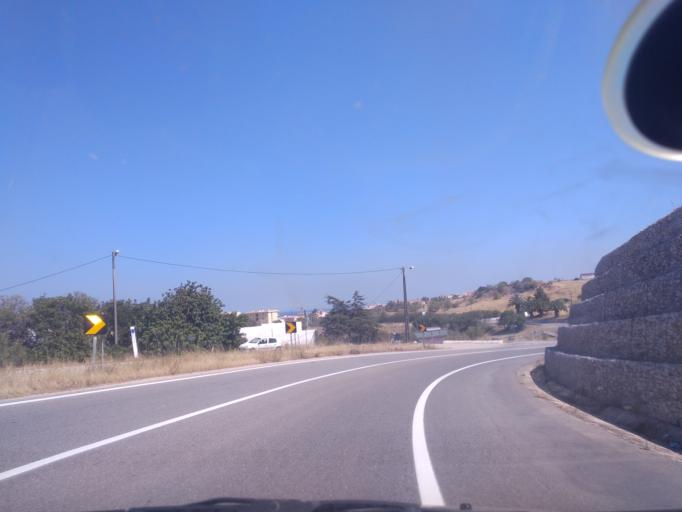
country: PT
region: Faro
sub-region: Lagos
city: Lagos
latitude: 37.1158
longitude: -8.6867
